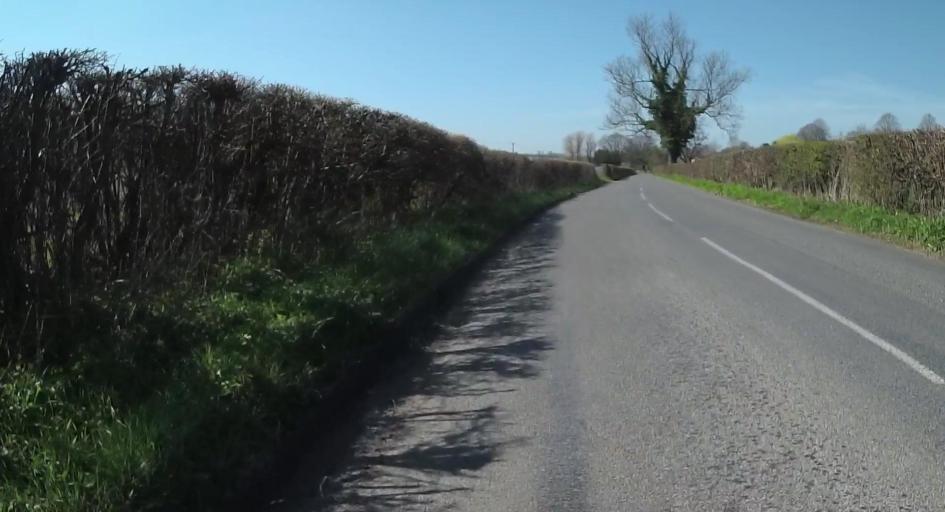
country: GB
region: England
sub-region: Hampshire
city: Andover
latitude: 51.2686
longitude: -1.4331
